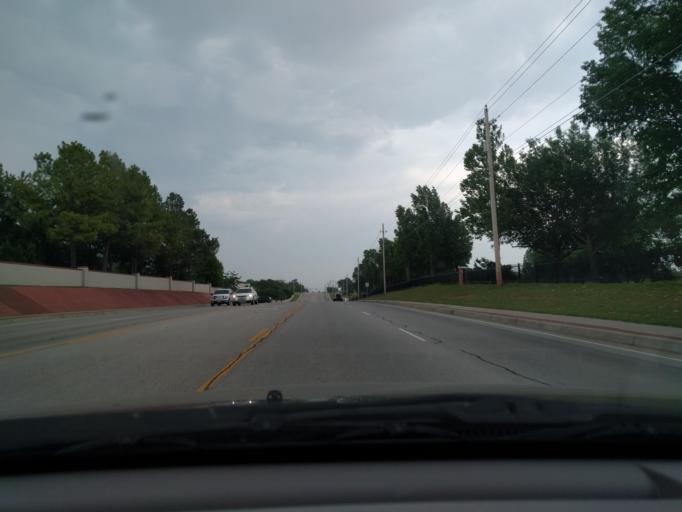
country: US
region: Oklahoma
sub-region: Tulsa County
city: Broken Arrow
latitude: 36.0463
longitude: -95.8773
